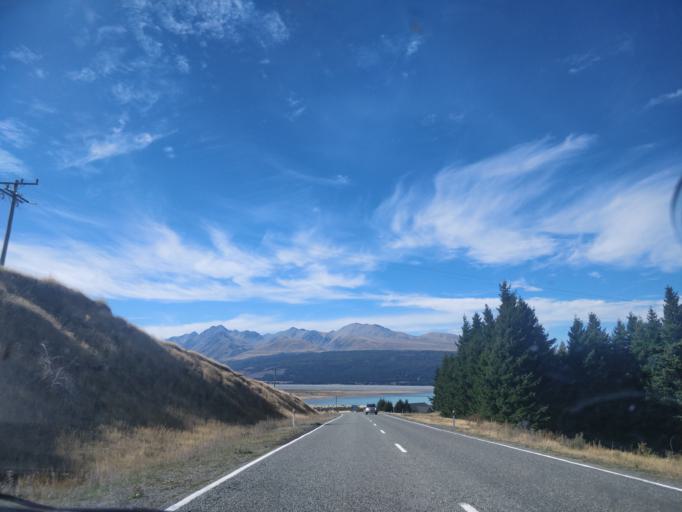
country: NZ
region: Canterbury
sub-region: Timaru District
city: Pleasant Point
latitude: -43.9132
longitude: 170.1178
